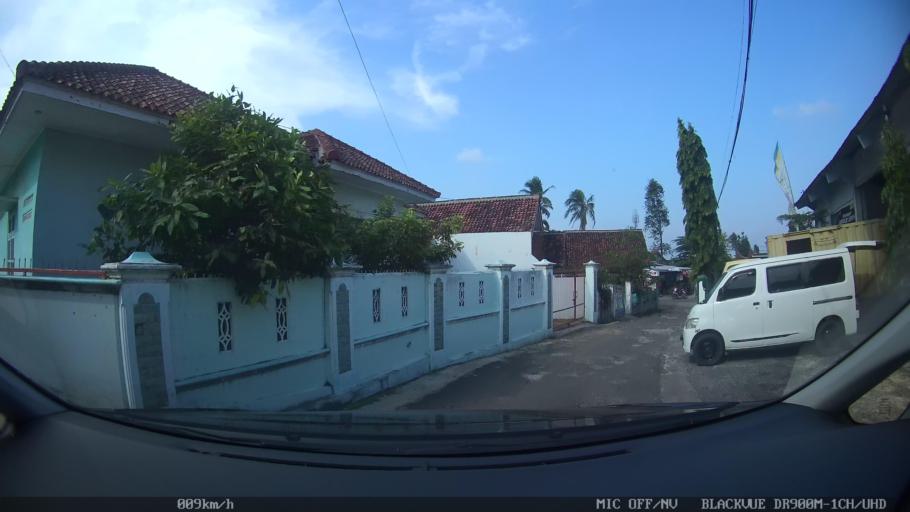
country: ID
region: Lampung
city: Kedaton
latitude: -5.3869
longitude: 105.2219
